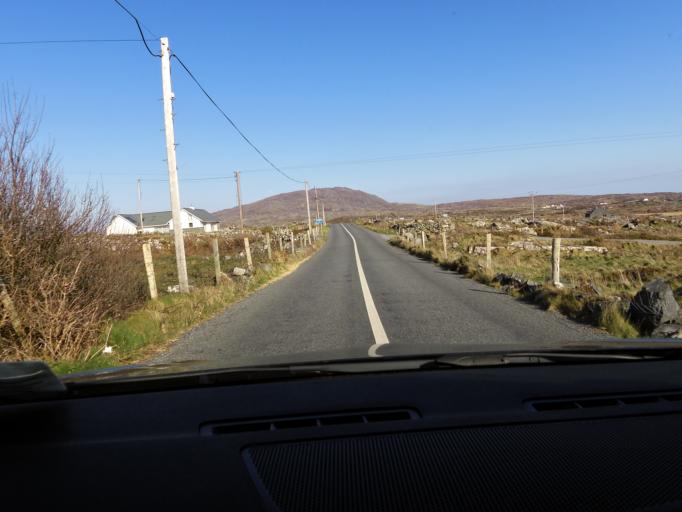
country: IE
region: Connaught
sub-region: County Galway
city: Clifden
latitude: 53.3952
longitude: -10.0154
